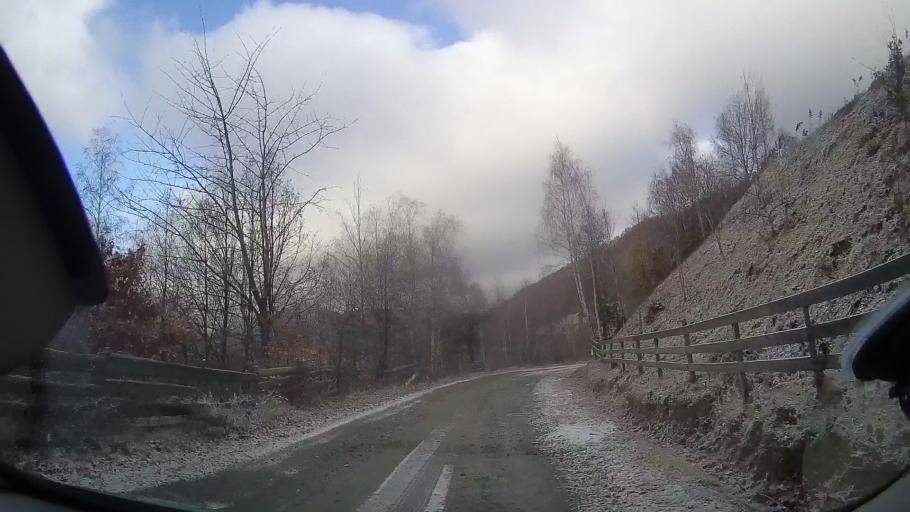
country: RO
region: Cluj
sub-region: Comuna Valea Ierii
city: Valea Ierii
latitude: 46.6743
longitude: 23.3210
